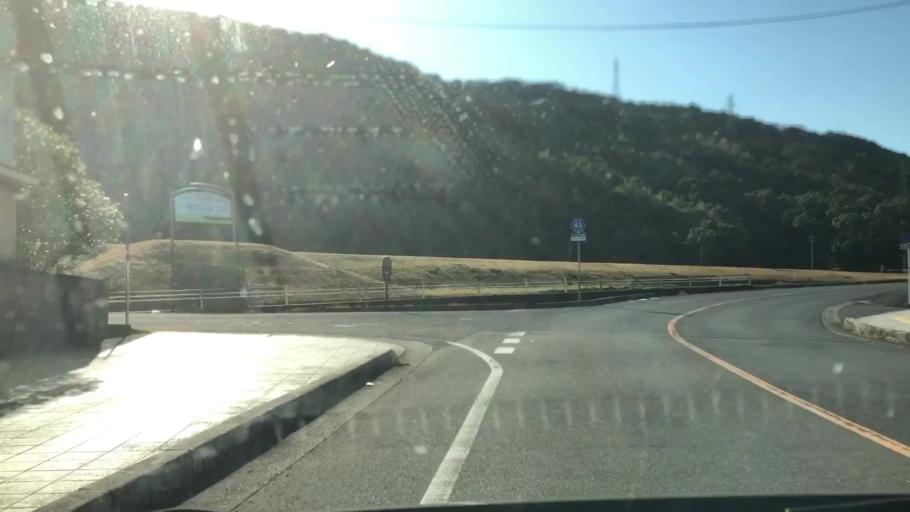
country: JP
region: Kagoshima
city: Satsumasendai
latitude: 31.8144
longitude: 130.2999
